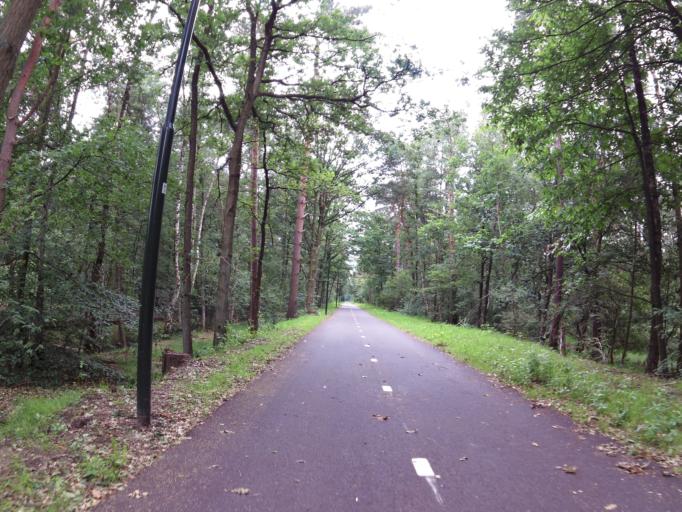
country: NL
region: North Brabant
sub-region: Gemeente Waalre
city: Waalre
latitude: 51.3735
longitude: 5.4605
